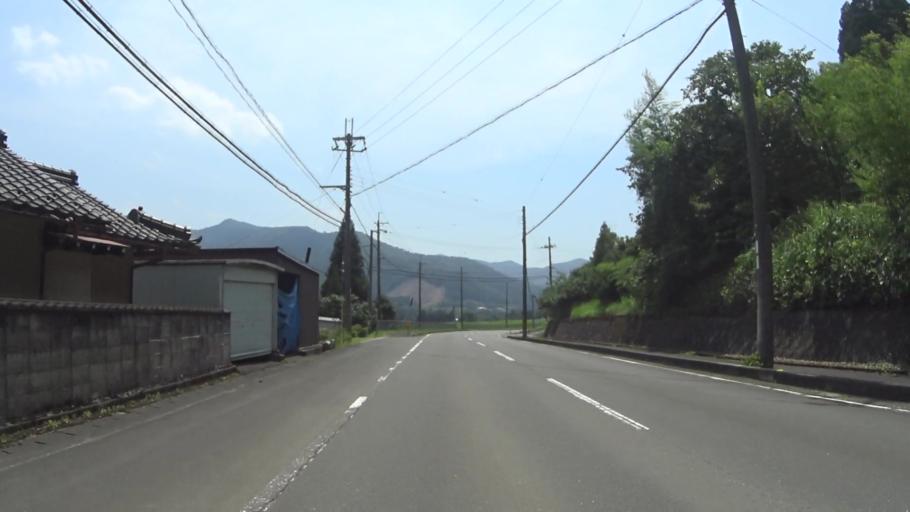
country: JP
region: Kyoto
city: Ayabe
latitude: 35.2743
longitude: 135.4320
